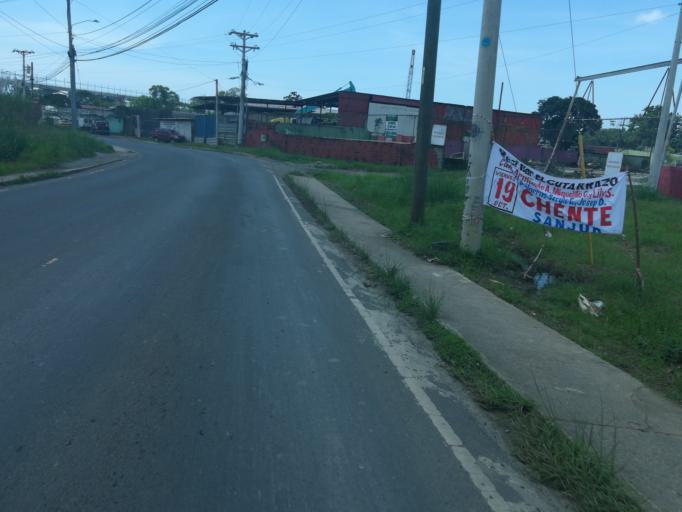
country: PA
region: Panama
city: Tocumen
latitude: 9.0863
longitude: -79.3992
